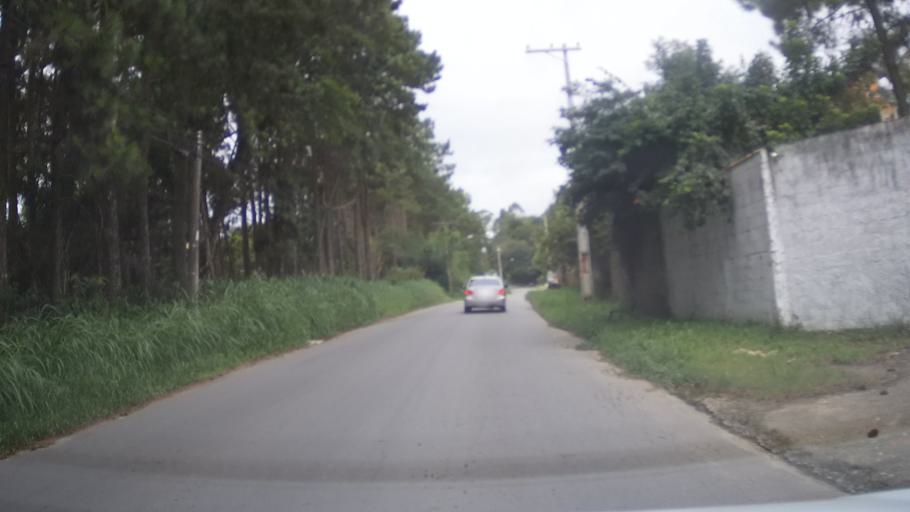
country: BR
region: Sao Paulo
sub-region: Aruja
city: Aruja
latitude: -23.3749
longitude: -46.3012
